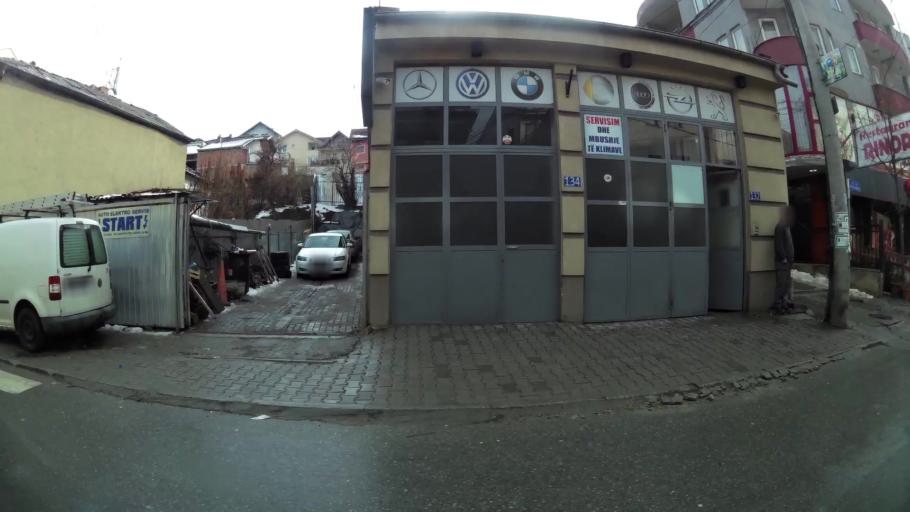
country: XK
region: Pristina
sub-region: Komuna e Prishtines
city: Pristina
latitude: 42.6706
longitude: 21.1711
